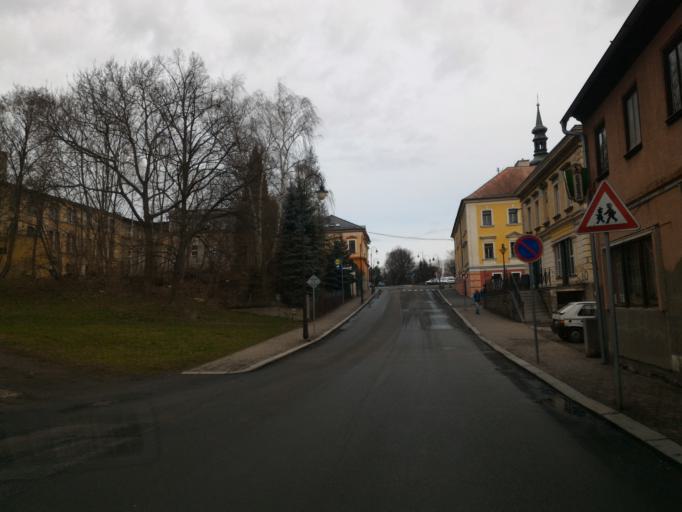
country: CZ
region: Ustecky
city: Varnsdorf
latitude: 50.9104
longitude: 14.6197
